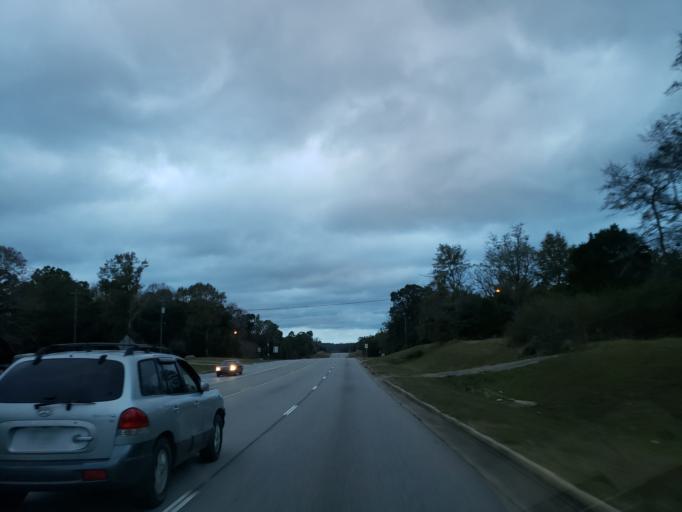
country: US
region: Alabama
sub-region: Mobile County
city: Chickasaw
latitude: 30.7951
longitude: -88.2254
